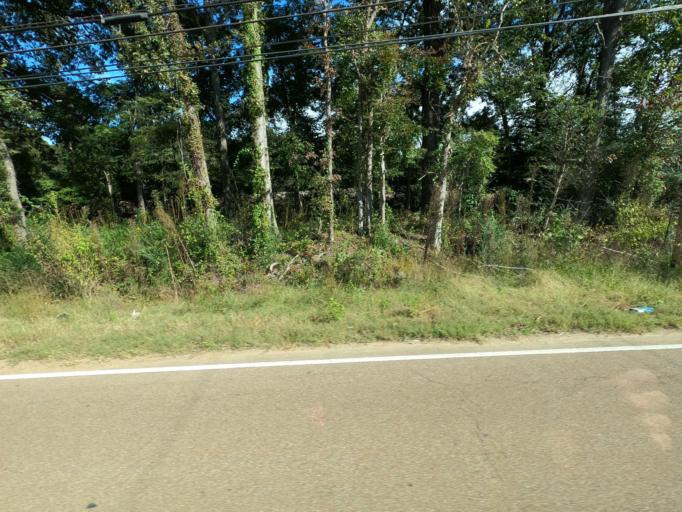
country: US
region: Tennessee
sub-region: Fayette County
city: Hickory Withe
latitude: 35.2118
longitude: -89.6506
